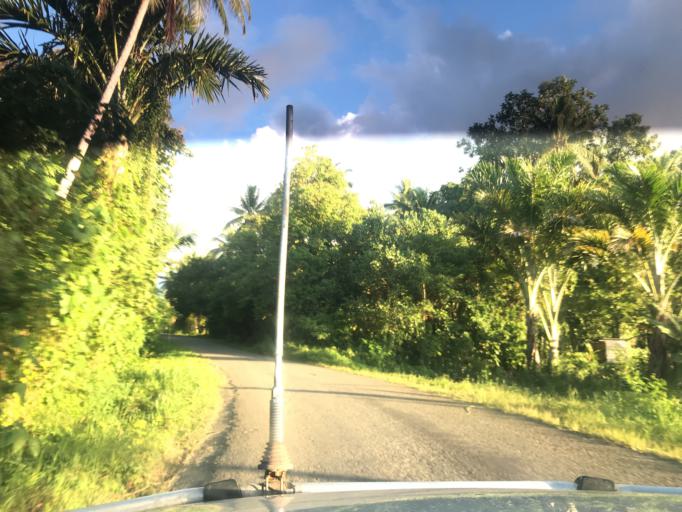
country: SB
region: Malaita
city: Auki
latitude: -8.7157
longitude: 160.7026
